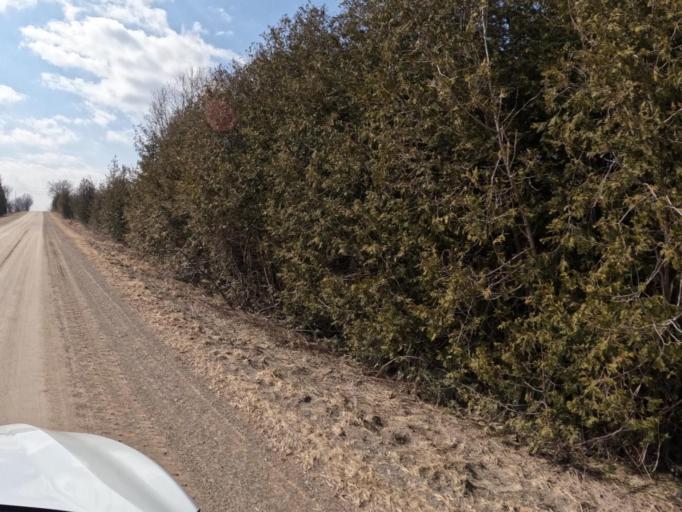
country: CA
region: Ontario
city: Orangeville
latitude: 43.9179
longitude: -80.2549
